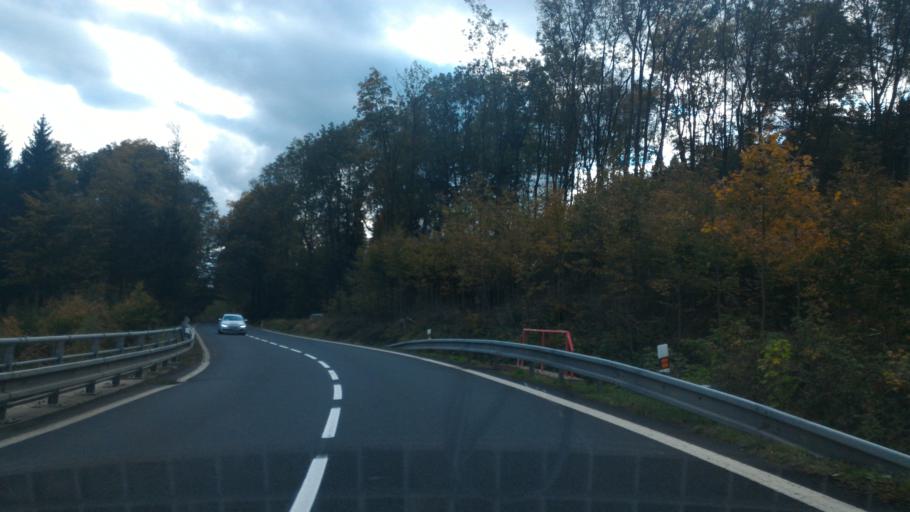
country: CZ
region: Ustecky
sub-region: Okres Decin
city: Chribska
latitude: 50.8227
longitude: 14.4721
